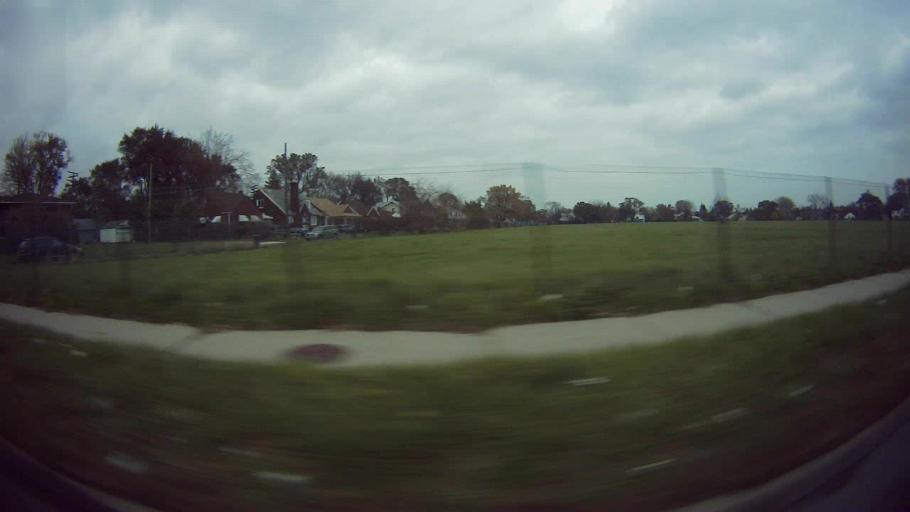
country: US
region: Michigan
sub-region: Wayne County
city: Hamtramck
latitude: 42.4088
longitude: -83.0024
